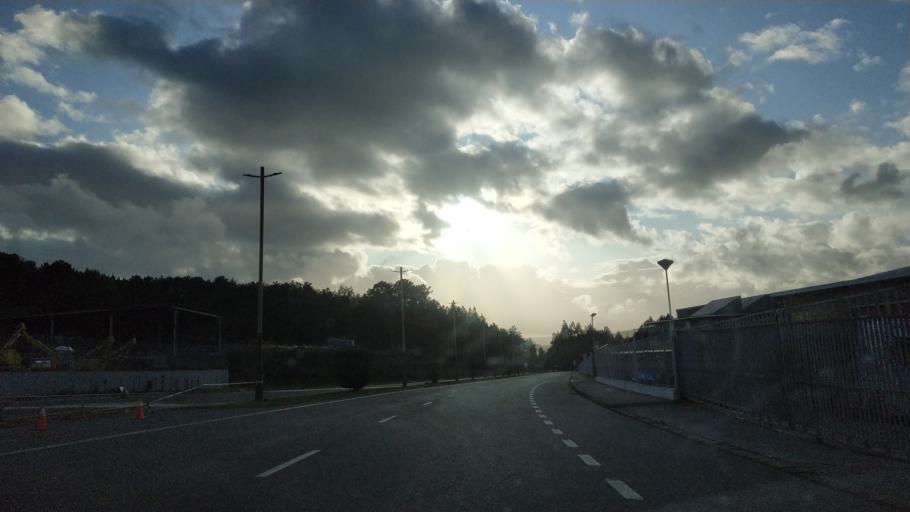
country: ES
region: Galicia
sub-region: Provincia de Pontevedra
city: Silleda
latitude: 42.7906
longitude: -8.1618
